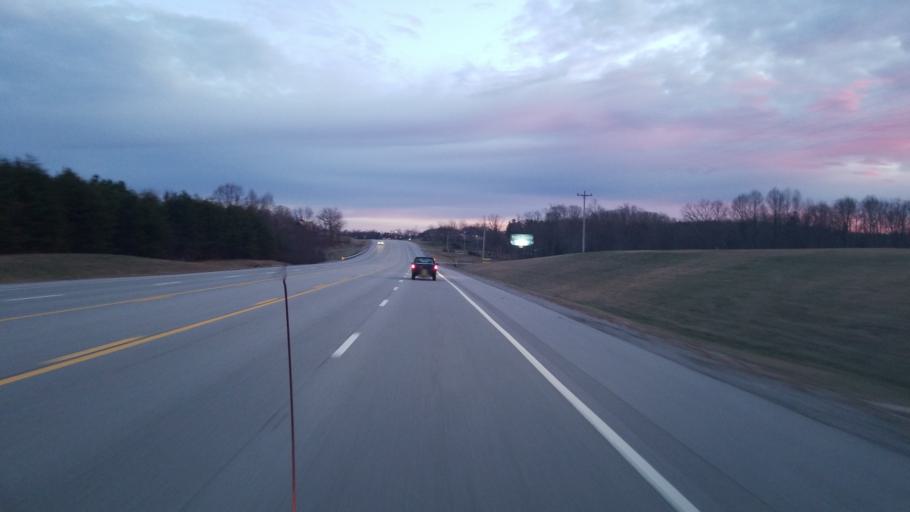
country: US
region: Tennessee
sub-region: Van Buren County
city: Spencer
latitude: 35.7334
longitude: -85.4616
